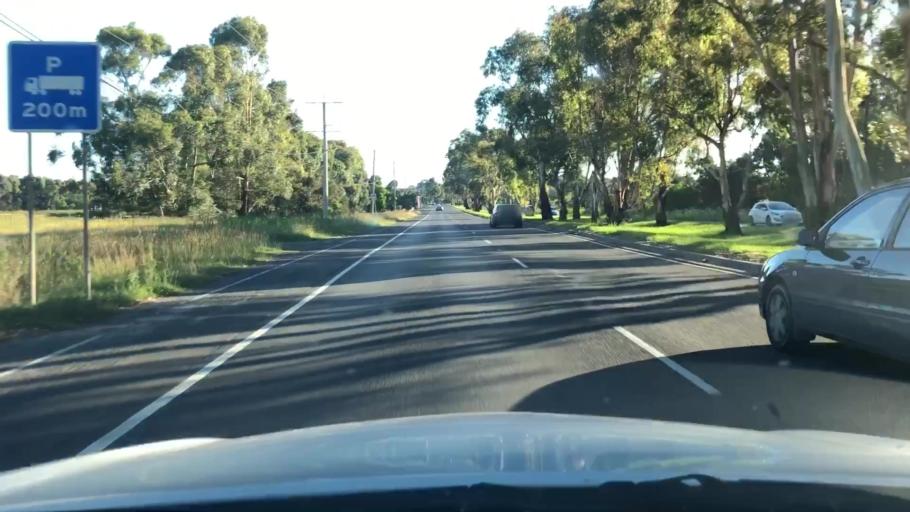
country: AU
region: Victoria
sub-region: Knox
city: Rowville
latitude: -37.9467
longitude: 145.2292
